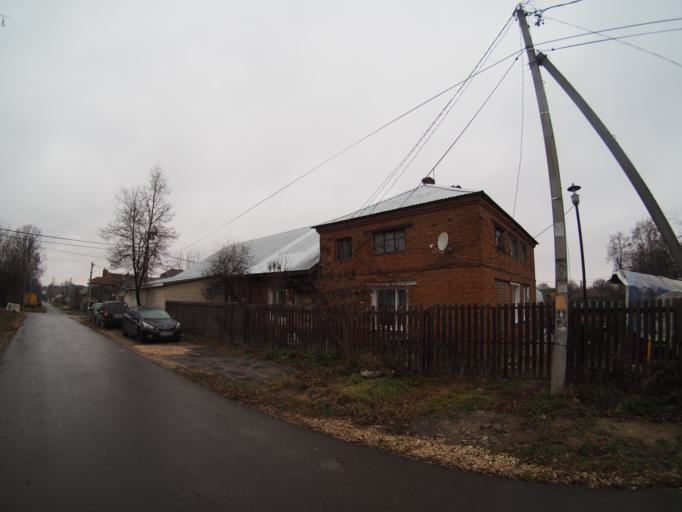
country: RU
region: Moskovskaya
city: Mikhnevo
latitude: 55.1247
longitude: 37.9528
